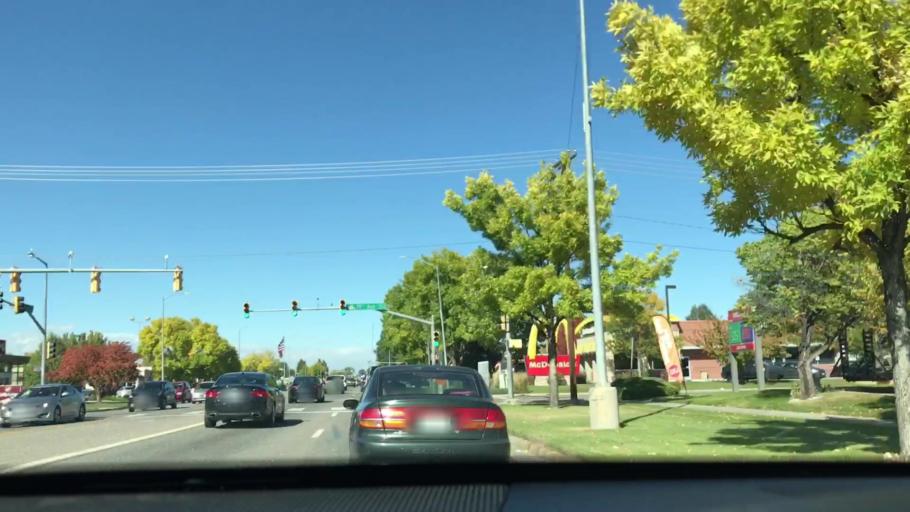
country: US
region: Colorado
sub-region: Boulder County
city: Longmont
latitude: 40.1918
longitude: -105.1022
